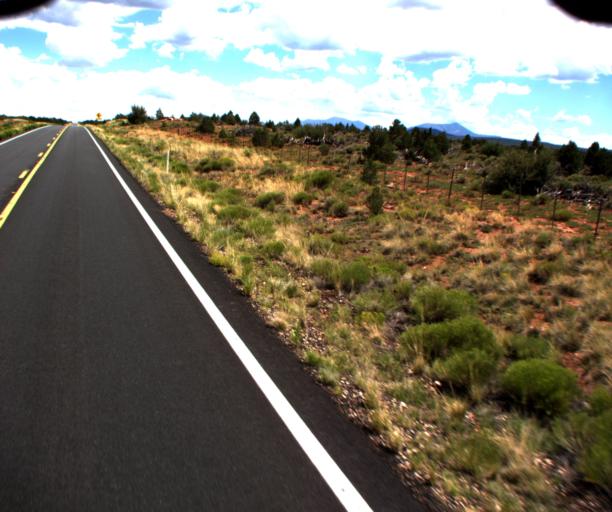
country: US
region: Arizona
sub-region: Coconino County
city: Parks
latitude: 35.6031
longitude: -112.0355
